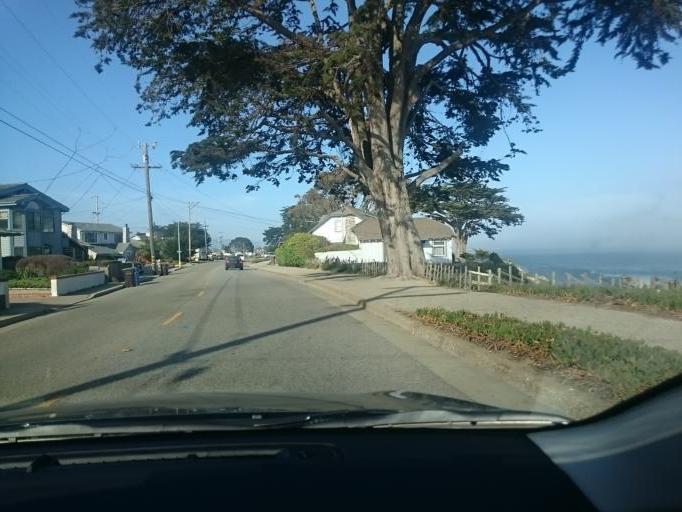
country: US
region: California
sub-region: Santa Cruz County
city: Santa Cruz
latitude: 36.9504
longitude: -122.0453
